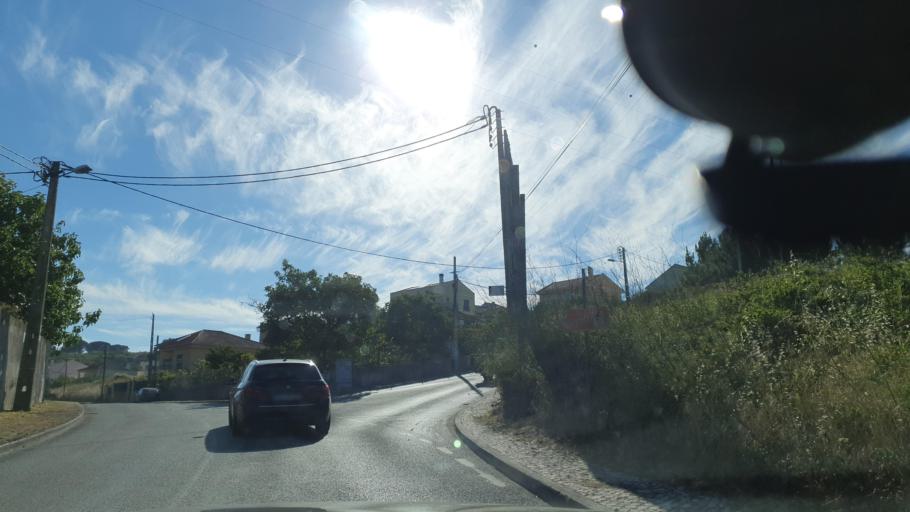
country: PT
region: Lisbon
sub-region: Sintra
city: Belas
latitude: 38.7962
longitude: -9.2480
